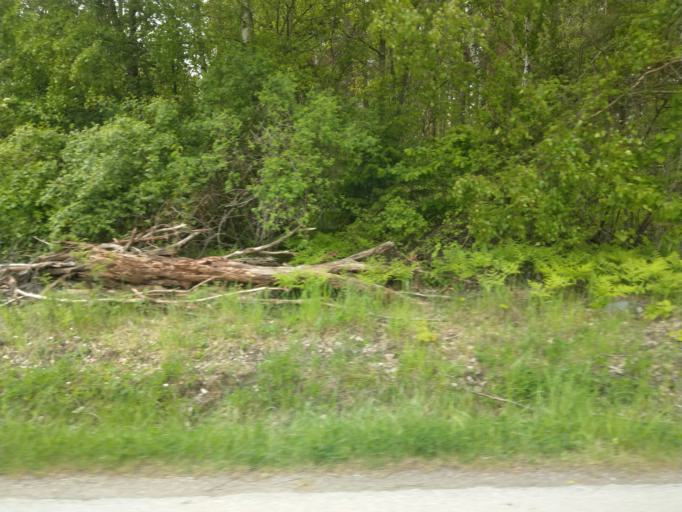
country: SE
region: Stockholm
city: Stenhamra
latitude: 59.4104
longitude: 17.6215
